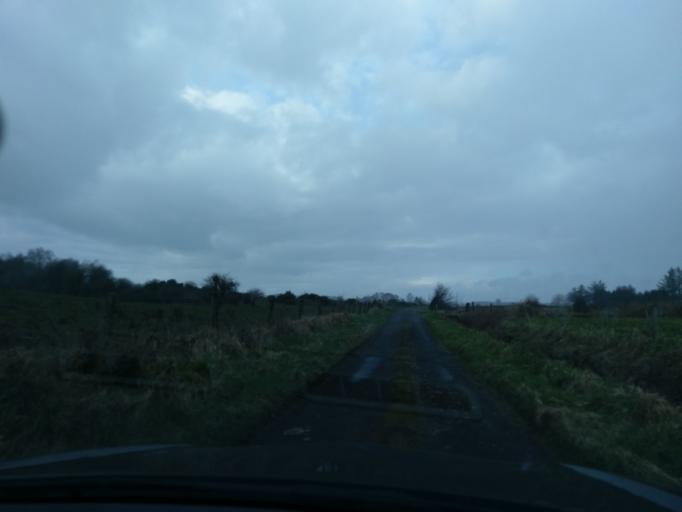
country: IE
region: Connaught
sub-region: County Galway
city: Athenry
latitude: 53.4013
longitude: -8.6062
